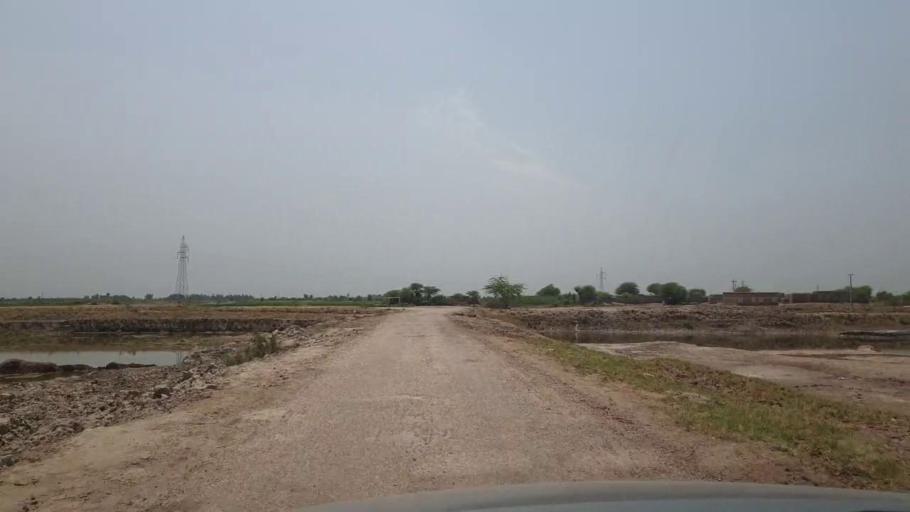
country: PK
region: Sindh
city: Garhi Yasin
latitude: 27.8907
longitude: 68.4935
